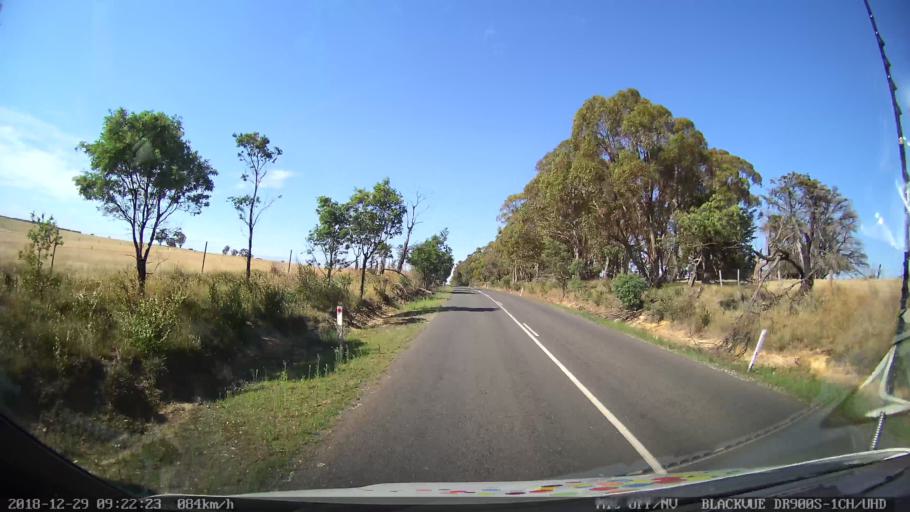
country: AU
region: New South Wales
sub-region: Upper Lachlan Shire
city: Crookwell
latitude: -34.5117
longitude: 149.4063
